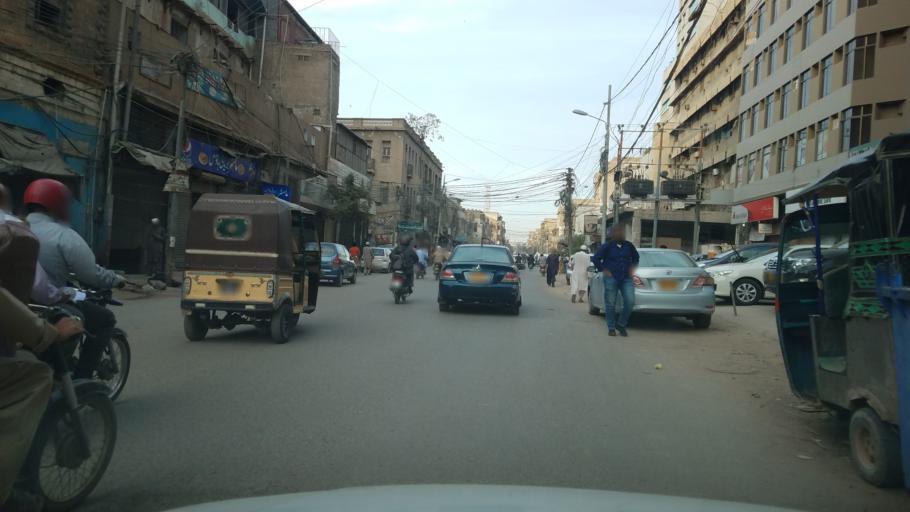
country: PK
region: Sindh
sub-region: Karachi District
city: Karachi
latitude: 24.8524
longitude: 67.0066
